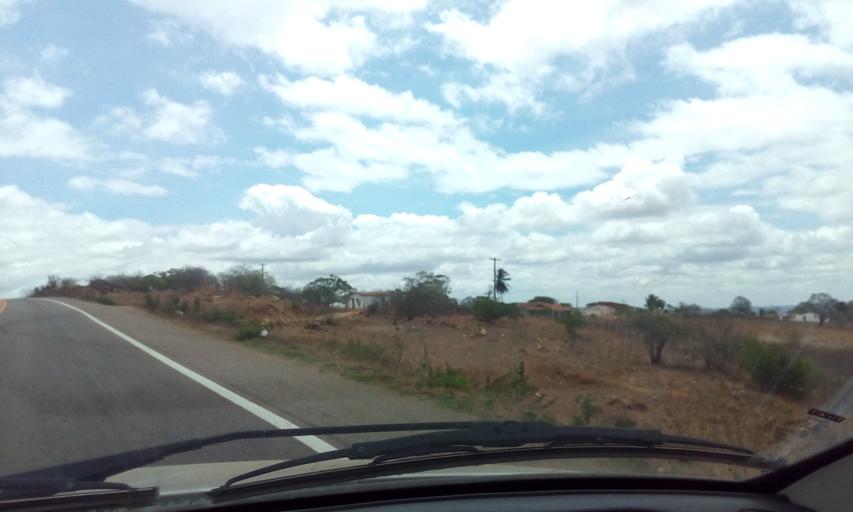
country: BR
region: Rio Grande do Norte
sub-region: Santa Cruz
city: Santa Cruz
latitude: -6.2167
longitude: -36.1723
